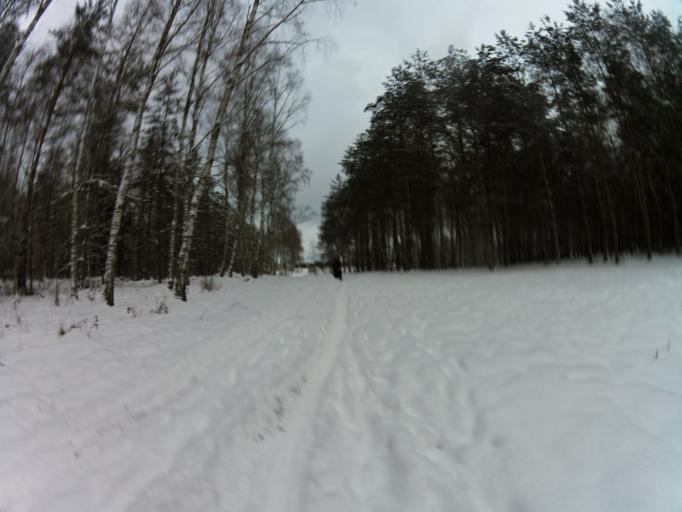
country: PL
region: West Pomeranian Voivodeship
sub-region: Powiat stargardzki
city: Insko
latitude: 53.3612
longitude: 15.5187
